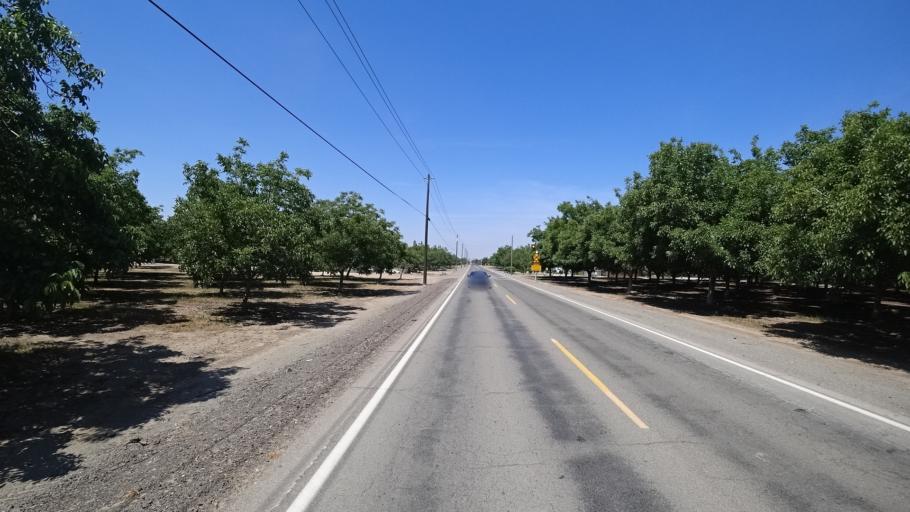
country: US
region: California
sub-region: Kings County
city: Lucerne
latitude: 36.4011
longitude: -119.6600
